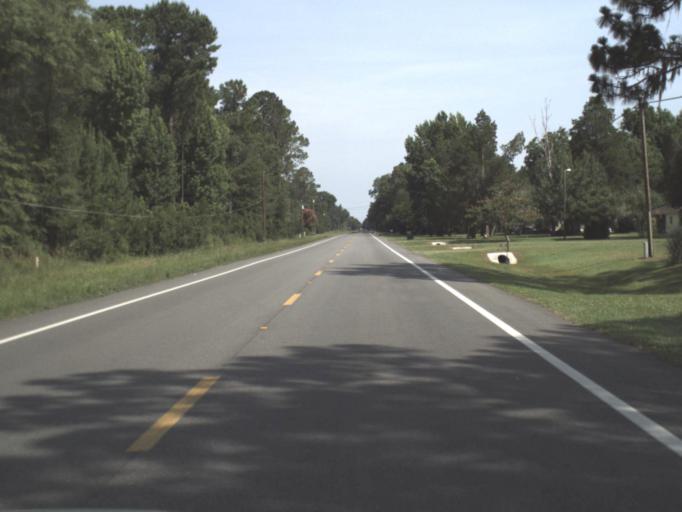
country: US
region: Florida
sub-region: Hamilton County
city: Jasper
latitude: 30.5338
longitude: -82.9708
